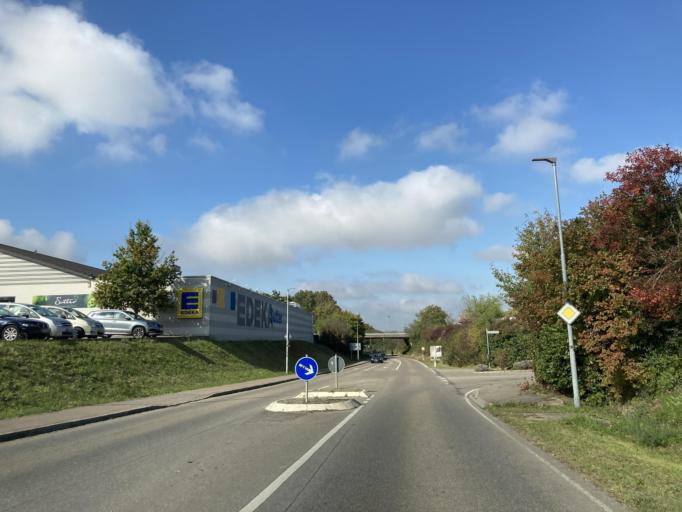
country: DE
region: Baden-Wuerttemberg
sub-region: Freiburg Region
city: Buggingen
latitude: 47.8524
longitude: 7.6342
